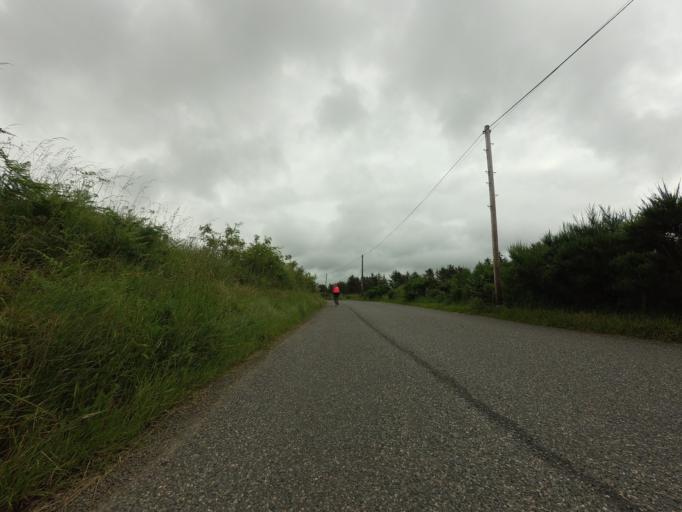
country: GB
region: Scotland
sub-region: Aberdeenshire
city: Turriff
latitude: 57.5352
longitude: -2.3744
